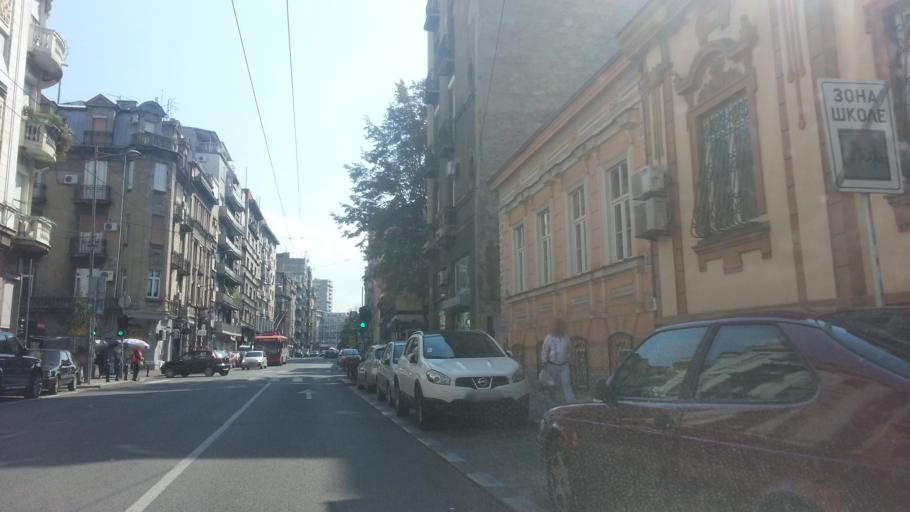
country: RS
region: Central Serbia
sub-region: Belgrade
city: Stari Grad
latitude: 44.8138
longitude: 20.4684
